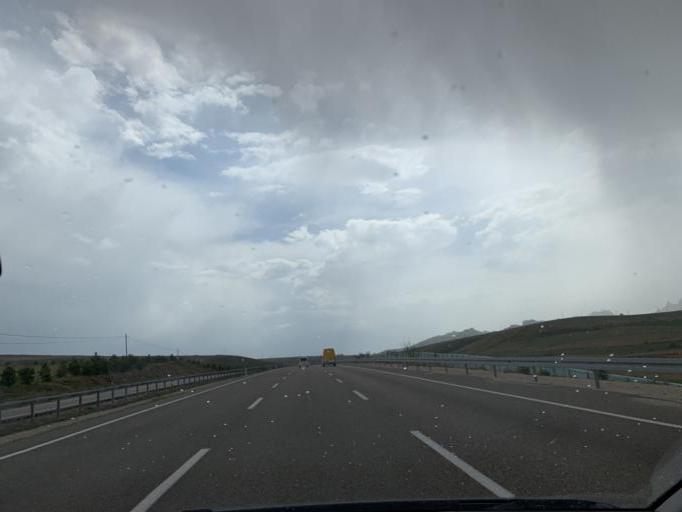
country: TR
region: Eskisehir
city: Sivrihisar
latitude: 39.4771
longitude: 31.5929
